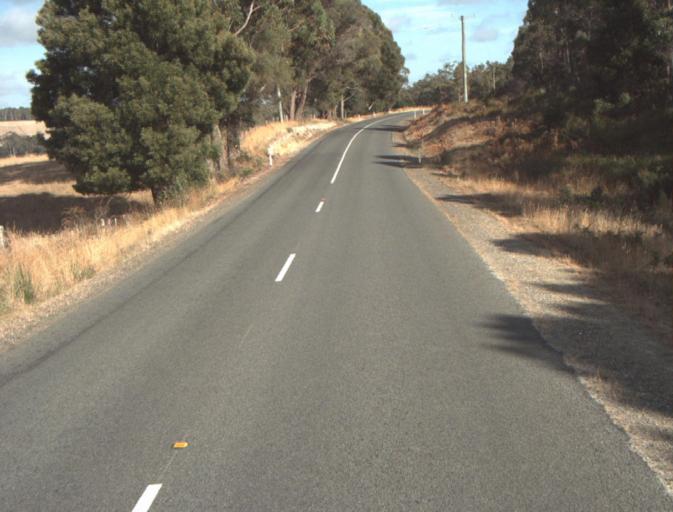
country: AU
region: Tasmania
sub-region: Dorset
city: Bridport
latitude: -41.1312
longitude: 147.2155
